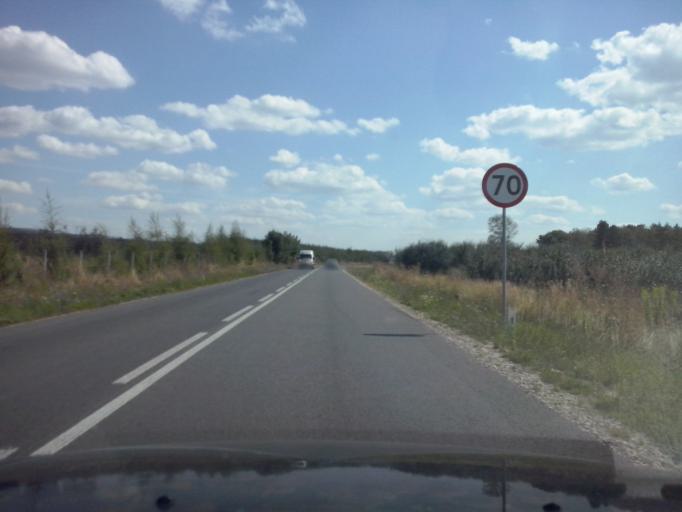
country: PL
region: Swietokrzyskie
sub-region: Powiat staszowski
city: Szydlow
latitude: 50.5851
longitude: 21.0533
